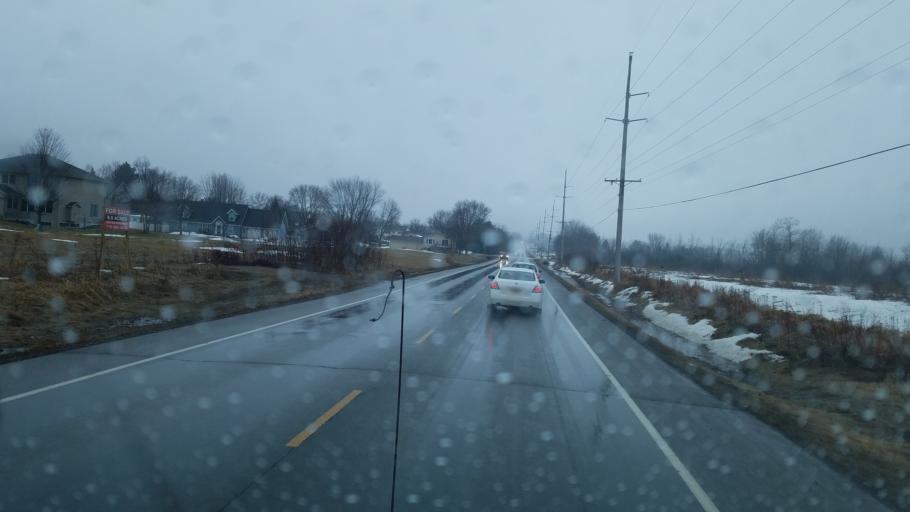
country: US
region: Wisconsin
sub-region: Wood County
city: Marshfield
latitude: 44.6791
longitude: -90.1983
